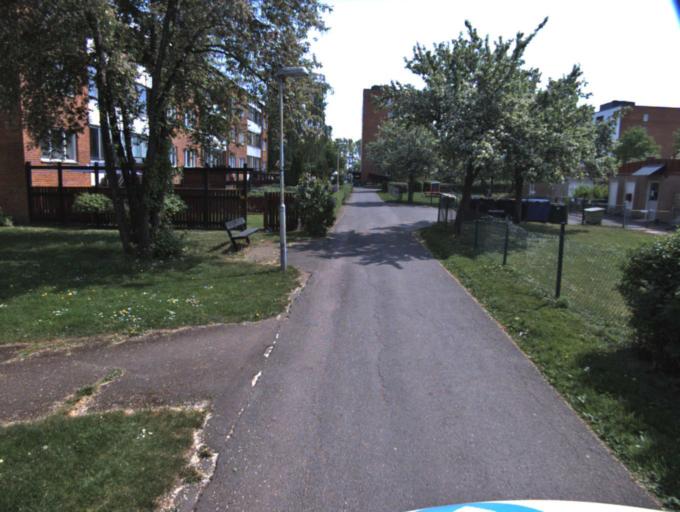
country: SE
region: Skane
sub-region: Kristianstads Kommun
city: Kristianstad
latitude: 56.0579
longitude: 14.1601
